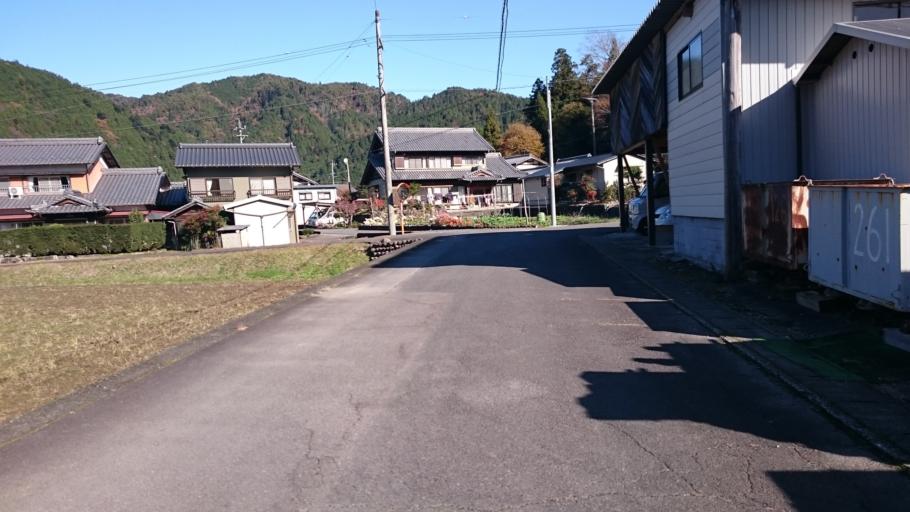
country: JP
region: Gifu
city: Minokamo
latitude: 35.6191
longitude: 137.1685
